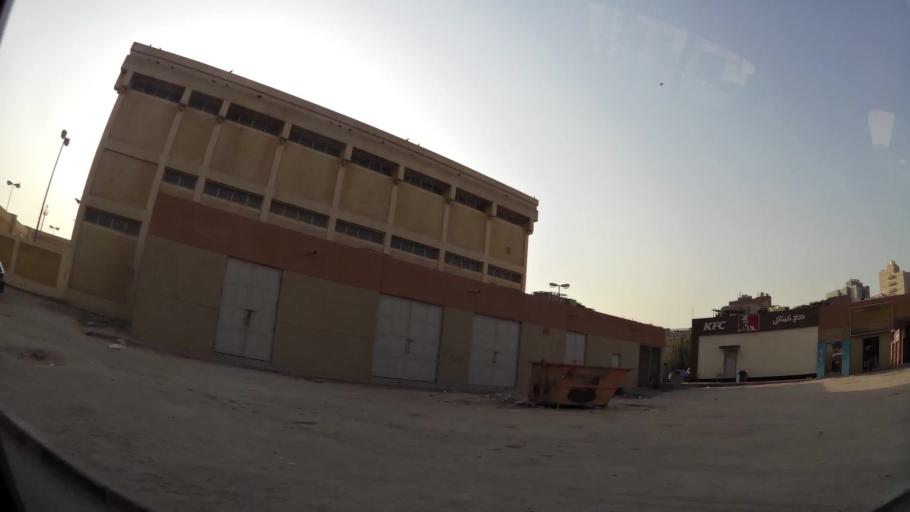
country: KW
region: Muhafazat Hawalli
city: As Salimiyah
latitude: 29.3278
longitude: 48.0672
